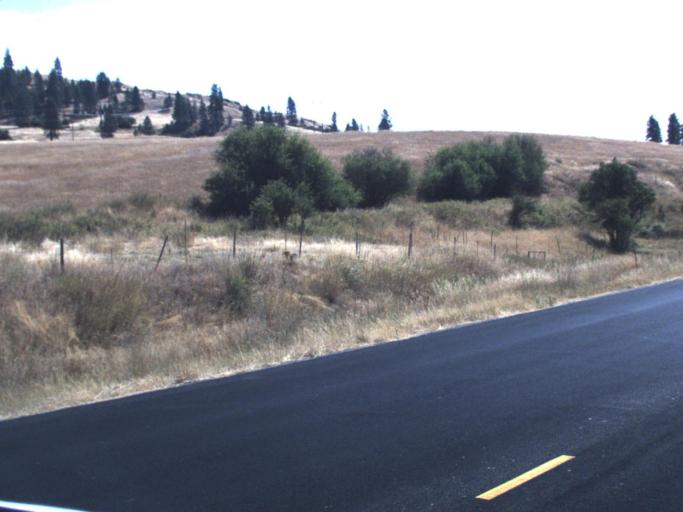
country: US
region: Washington
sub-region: Stevens County
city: Colville
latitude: 48.4946
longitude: -117.9026
